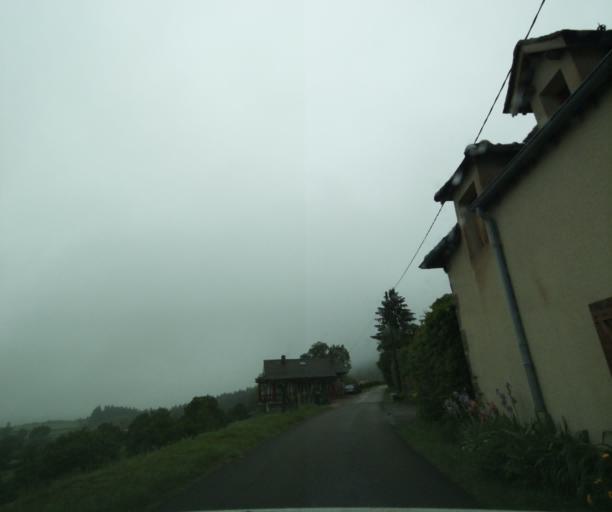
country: FR
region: Bourgogne
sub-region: Departement de Saone-et-Loire
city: Charolles
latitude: 46.4060
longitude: 4.4003
